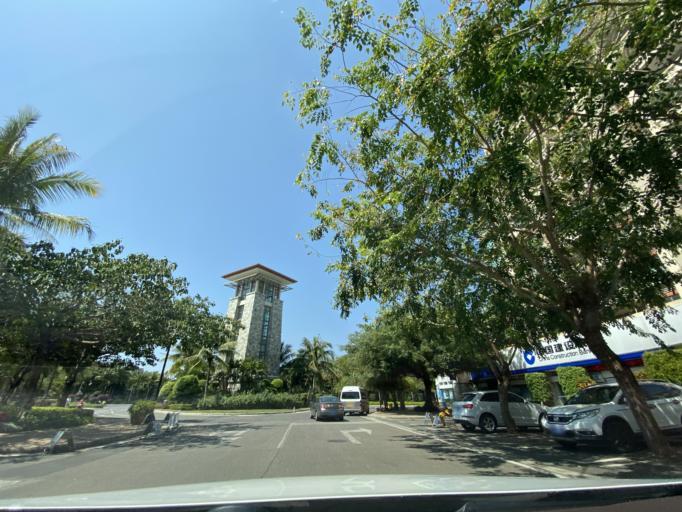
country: CN
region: Hainan
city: Yingzhou
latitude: 18.4078
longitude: 109.8492
